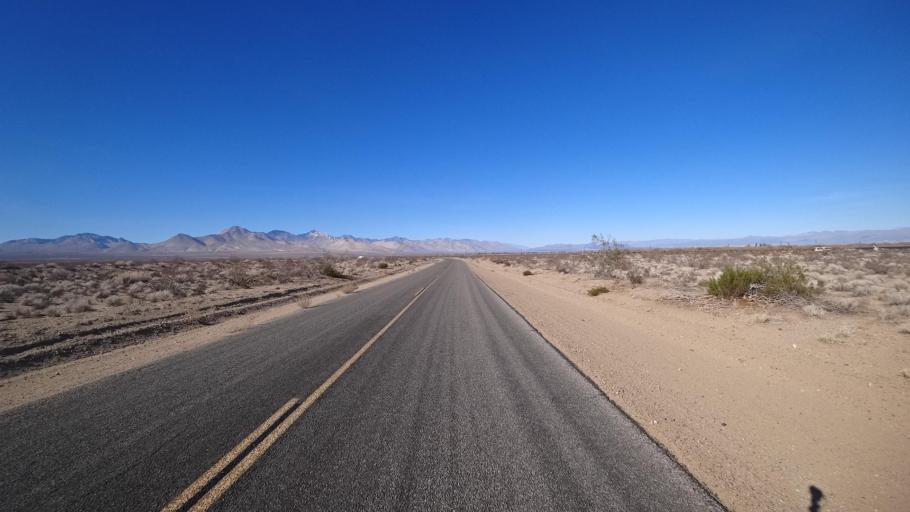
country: US
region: California
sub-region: Kern County
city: China Lake Acres
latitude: 35.5879
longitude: -117.7916
